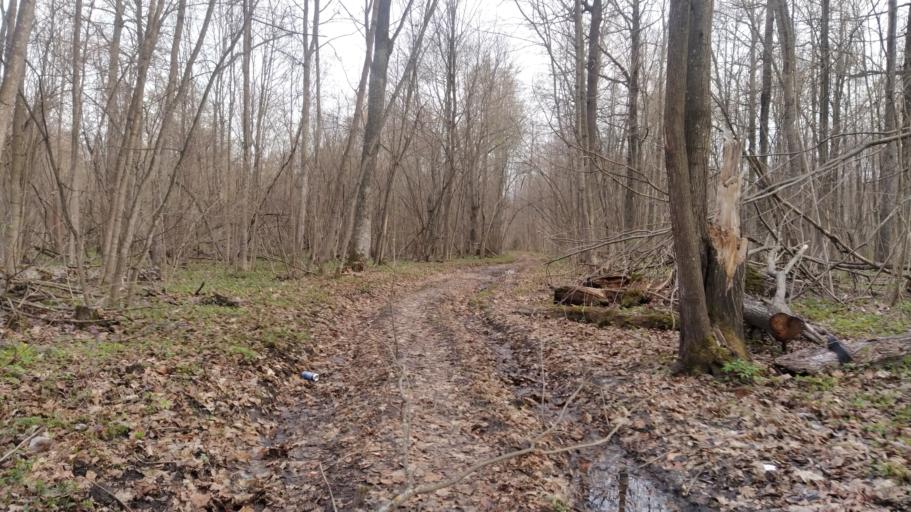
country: RU
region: Chuvashia
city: Novyye Lapsary
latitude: 56.1339
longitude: 47.1213
